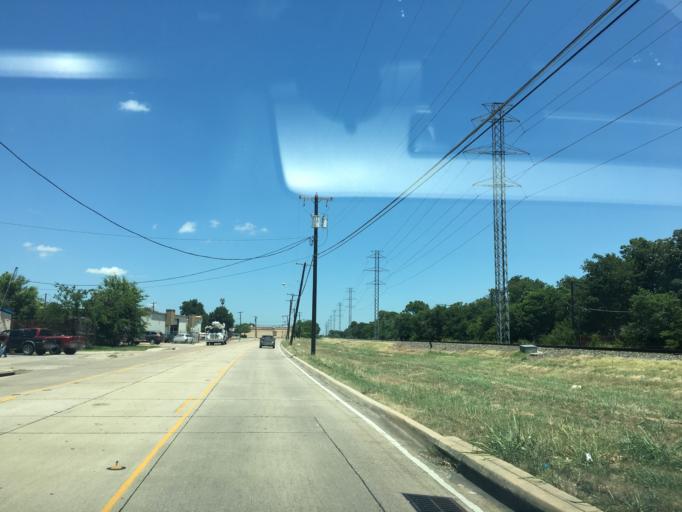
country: US
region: Texas
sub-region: Dallas County
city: Garland
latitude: 32.8447
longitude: -96.6845
